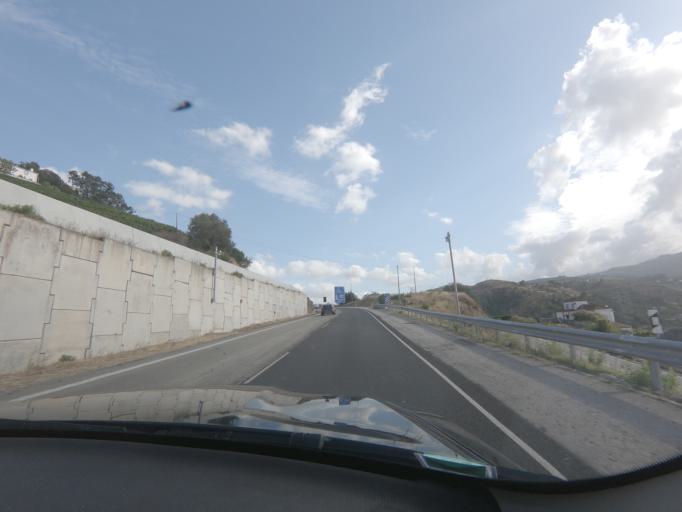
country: PT
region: Vila Real
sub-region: Peso da Regua
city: Peso da Regua
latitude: 41.1394
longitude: -7.7724
